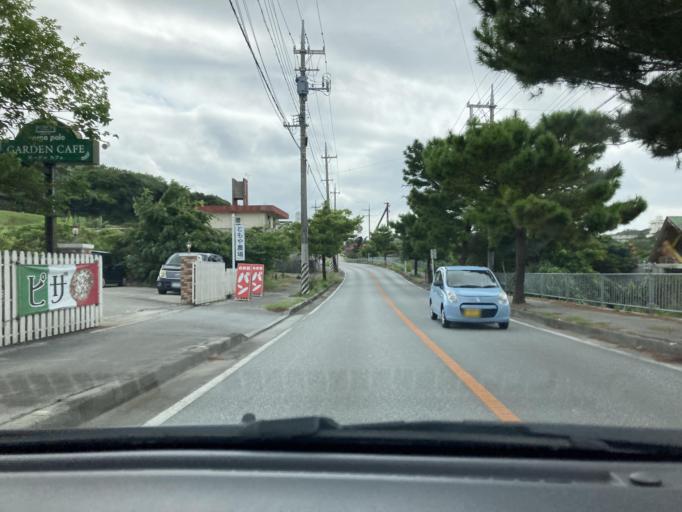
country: JP
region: Okinawa
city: Ginowan
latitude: 26.2650
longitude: 127.7751
